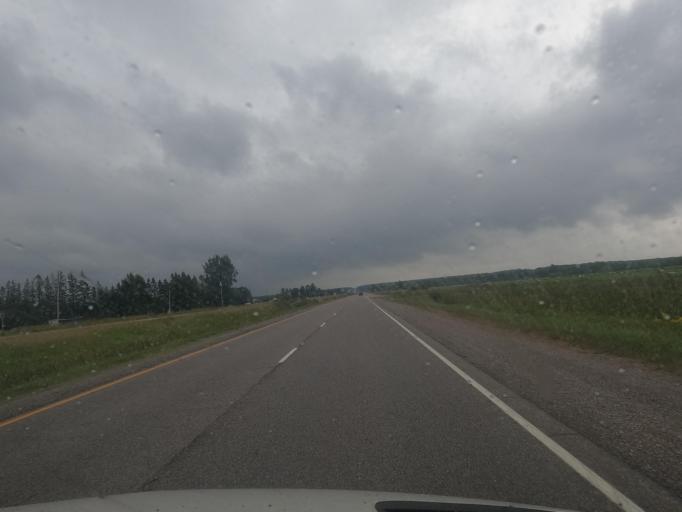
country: CA
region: Ontario
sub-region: Algoma
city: Sault Ste. Marie
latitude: 46.4390
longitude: -84.0683
